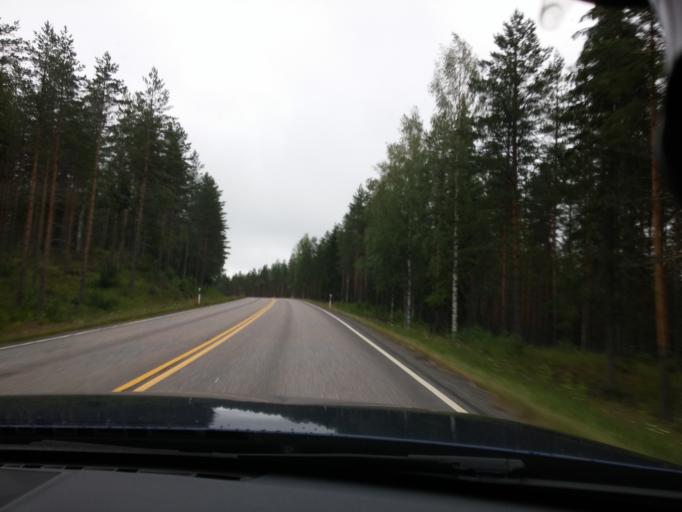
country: FI
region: Pirkanmaa
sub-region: Ylae-Pirkanmaa
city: Vilppula
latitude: 61.9256
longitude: 24.5417
